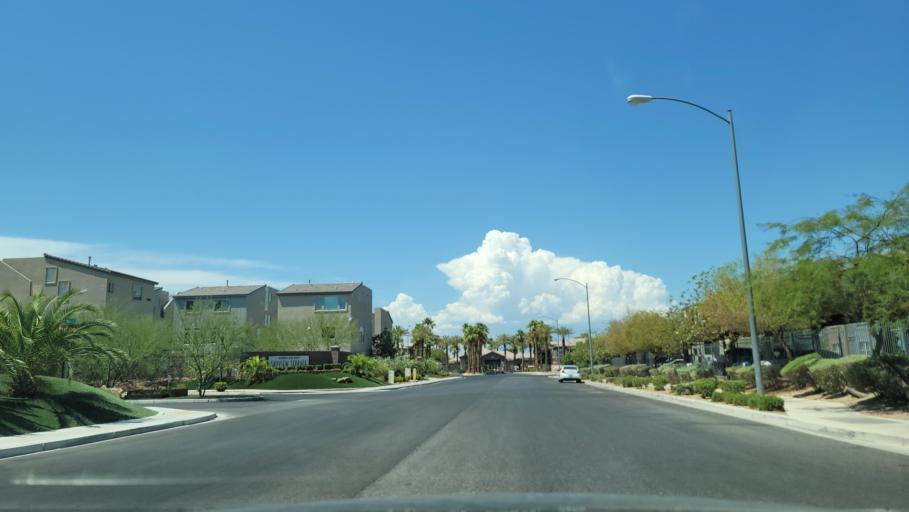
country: US
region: Nevada
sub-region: Clark County
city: Enterprise
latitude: 36.0598
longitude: -115.2655
